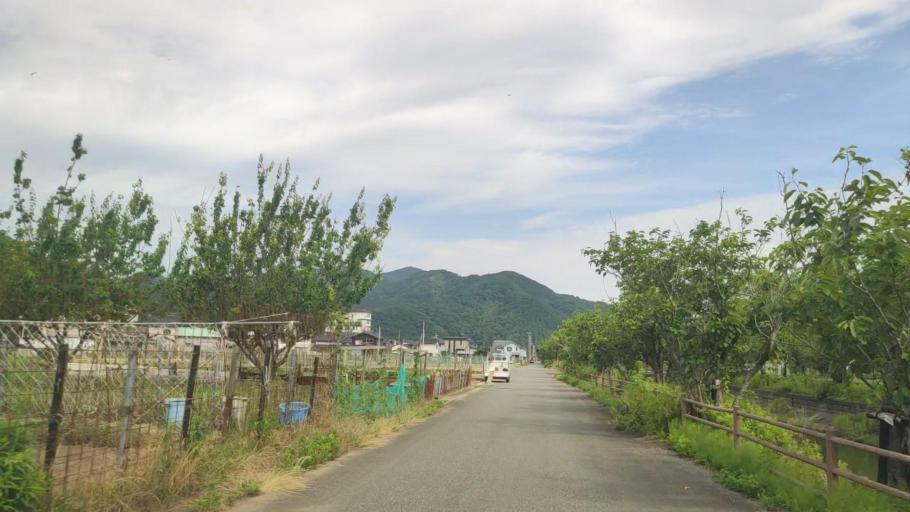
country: JP
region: Hyogo
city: Toyooka
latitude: 35.6400
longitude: 134.8390
